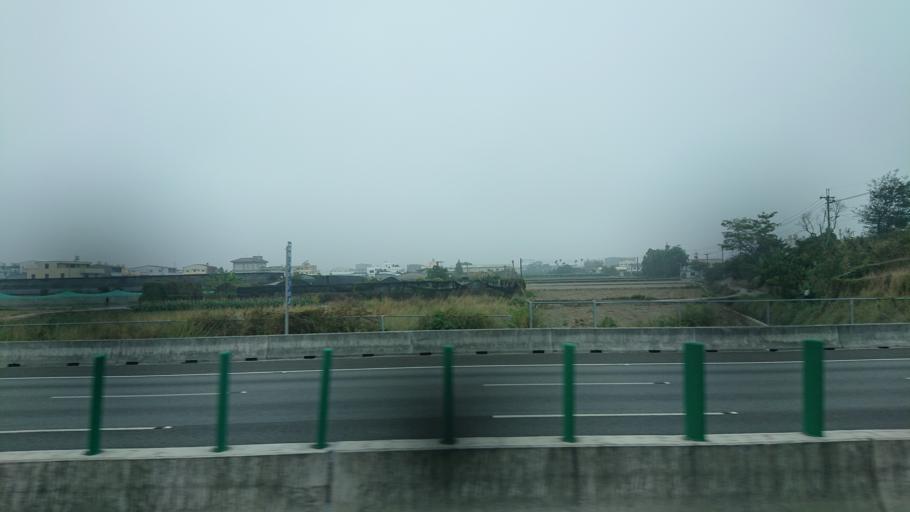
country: TW
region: Taiwan
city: Fengyuan
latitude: 24.3018
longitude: 120.6975
